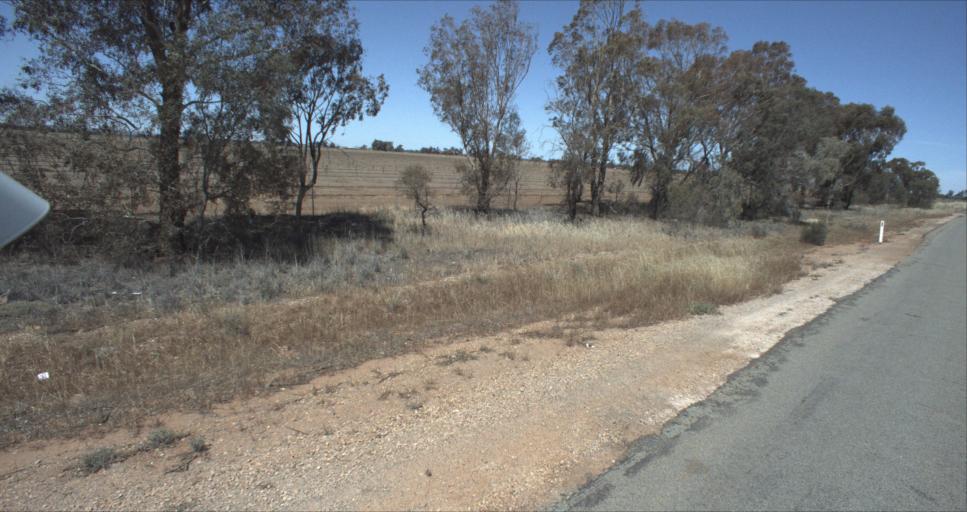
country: AU
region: New South Wales
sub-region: Leeton
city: Leeton
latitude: -34.5141
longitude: 146.3451
